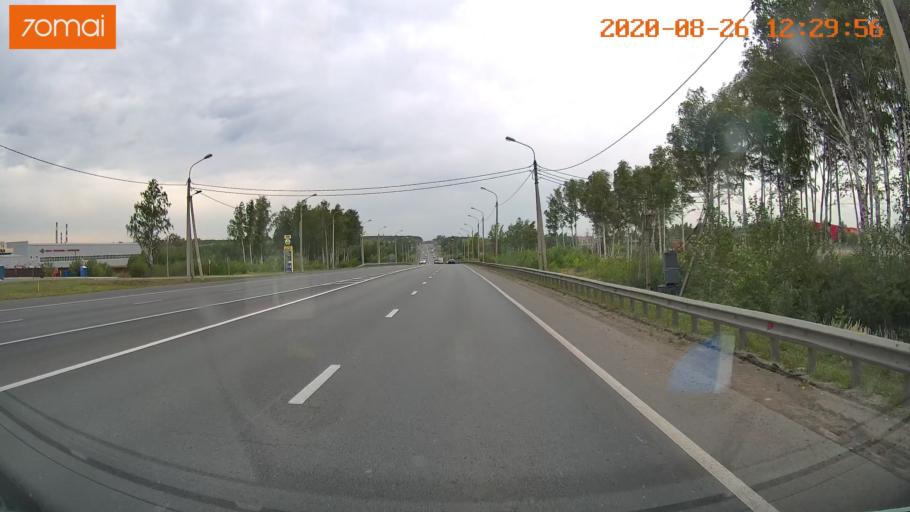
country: RU
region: Rjazan
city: Ryazan'
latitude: 54.5672
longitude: 39.8107
